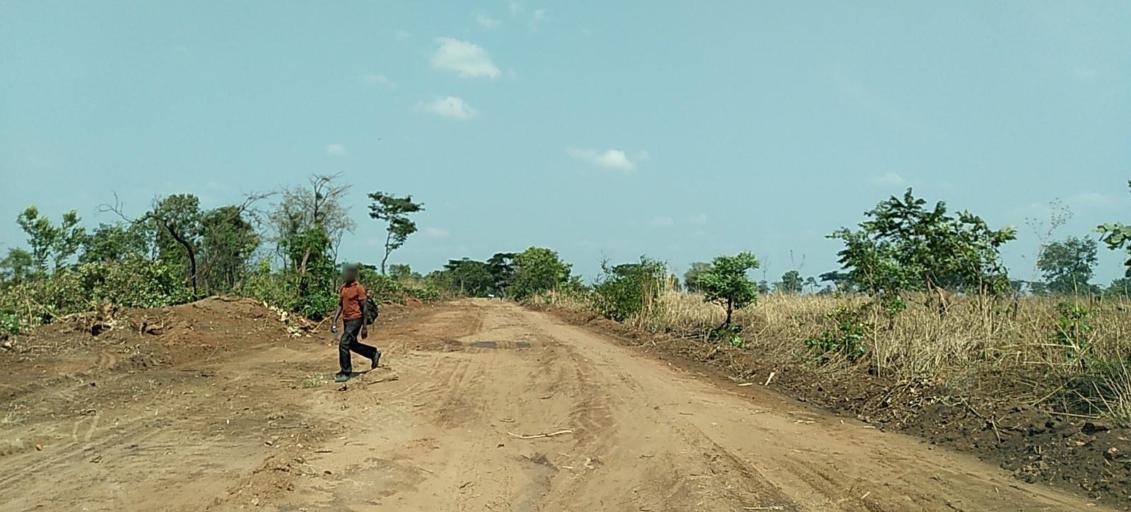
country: ZM
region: Copperbelt
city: Luanshya
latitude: -13.0894
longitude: 28.2637
